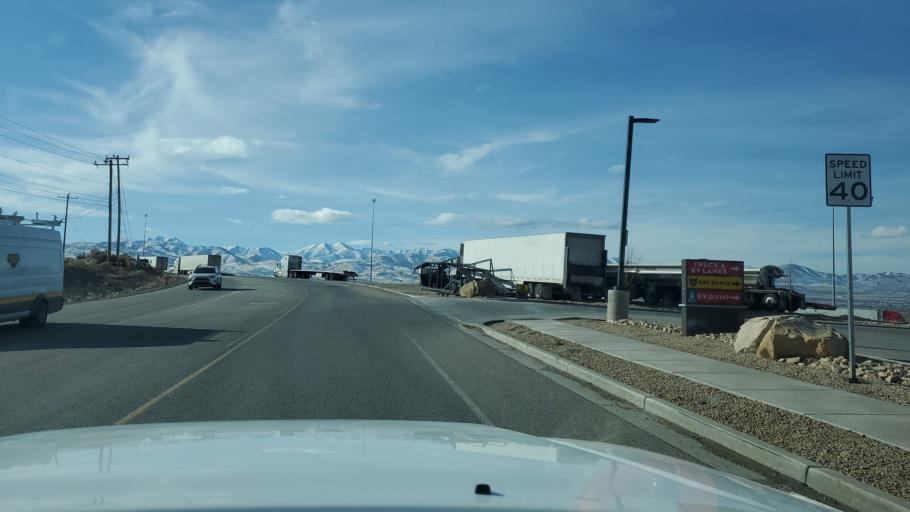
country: US
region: Utah
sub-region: Salt Lake County
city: Bluffdale
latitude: 40.4812
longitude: -111.8989
